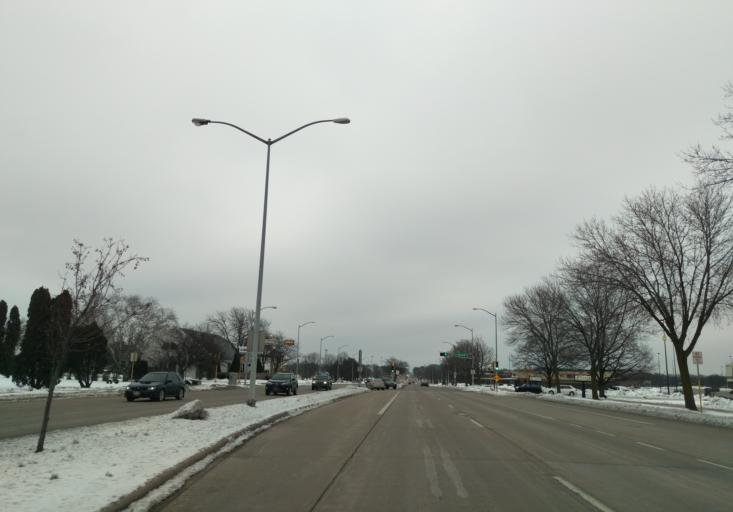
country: US
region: Wisconsin
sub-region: Dane County
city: Middleton
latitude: 43.0606
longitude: -89.5089
